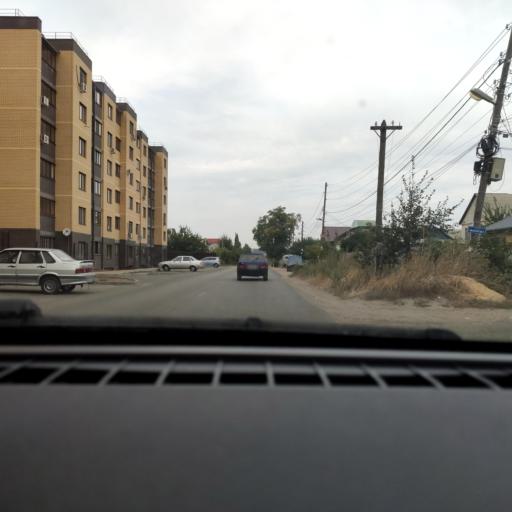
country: RU
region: Voronezj
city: Voronezh
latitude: 51.6657
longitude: 39.2806
